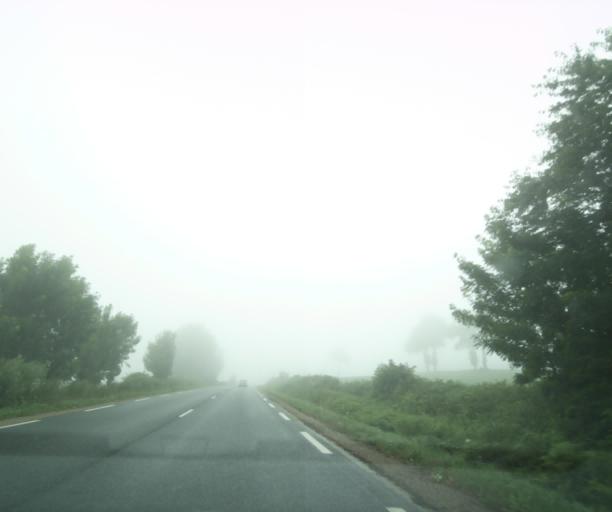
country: FR
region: Midi-Pyrenees
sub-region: Departement de l'Aveyron
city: Baraqueville
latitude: 44.2607
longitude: 2.4169
